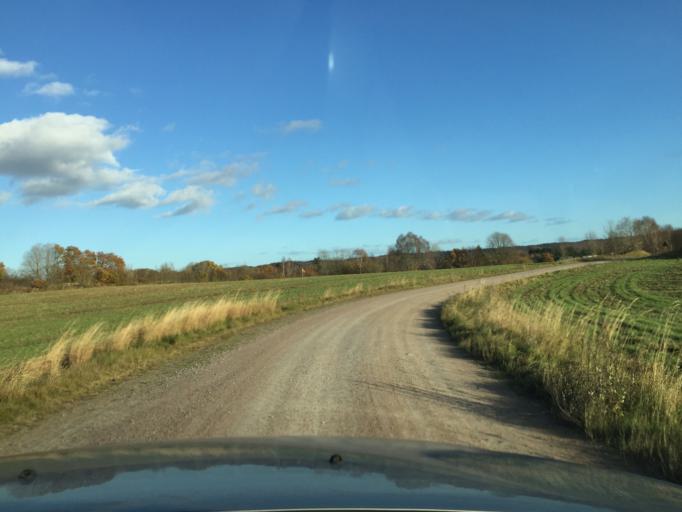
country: SE
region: Skane
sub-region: Hassleholms Kommun
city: Tormestorp
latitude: 56.0664
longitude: 13.7219
